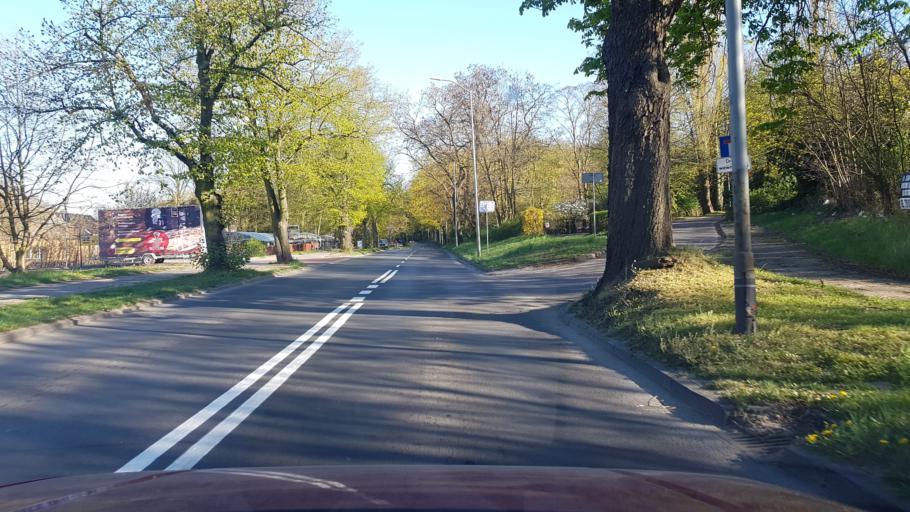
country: PL
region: West Pomeranian Voivodeship
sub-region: Szczecin
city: Szczecin
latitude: 53.3772
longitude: 14.6398
